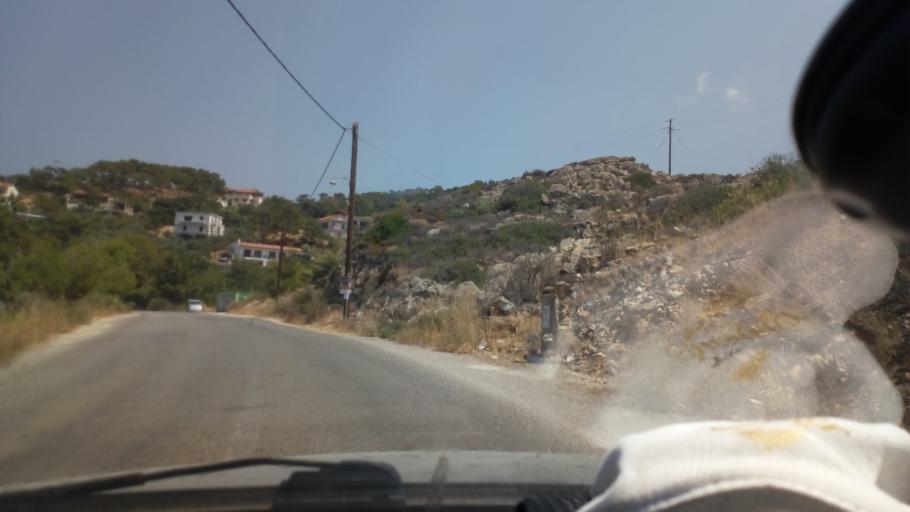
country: GR
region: North Aegean
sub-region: Nomos Samou
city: Agios Kirykos
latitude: 37.6292
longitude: 26.1008
